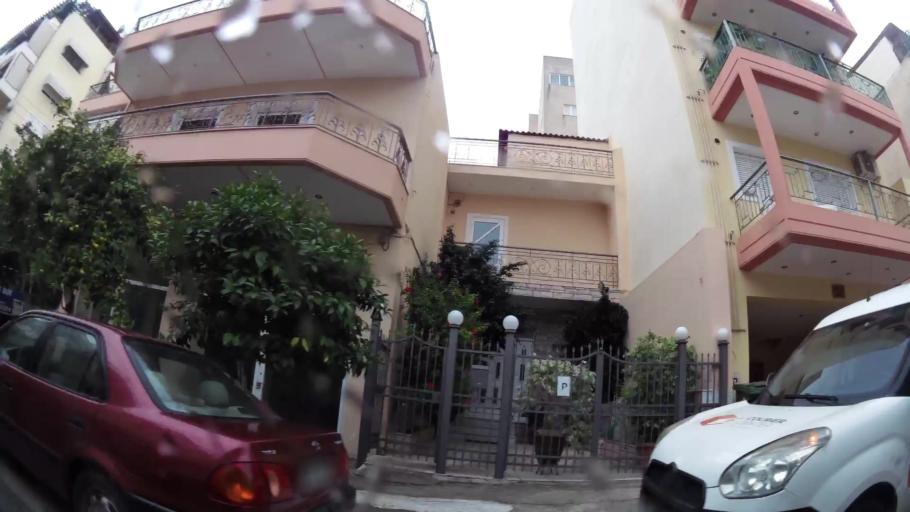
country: GR
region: Attica
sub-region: Nomos Piraios
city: Nikaia
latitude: 37.9608
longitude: 23.6473
